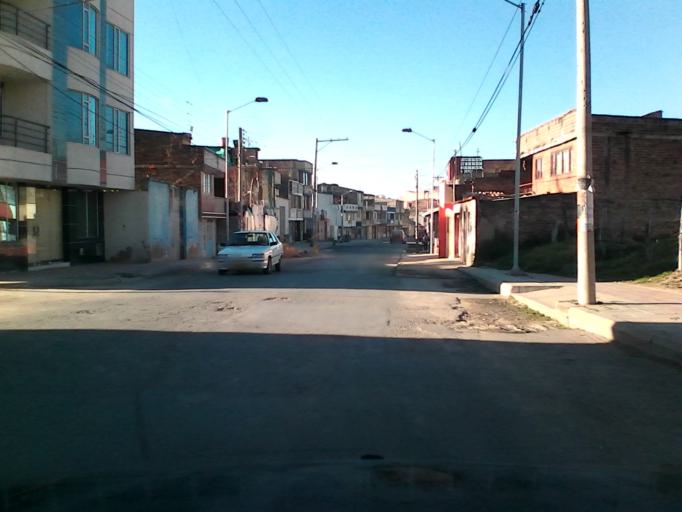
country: CO
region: Boyaca
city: Duitama
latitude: 5.8319
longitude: -73.0301
